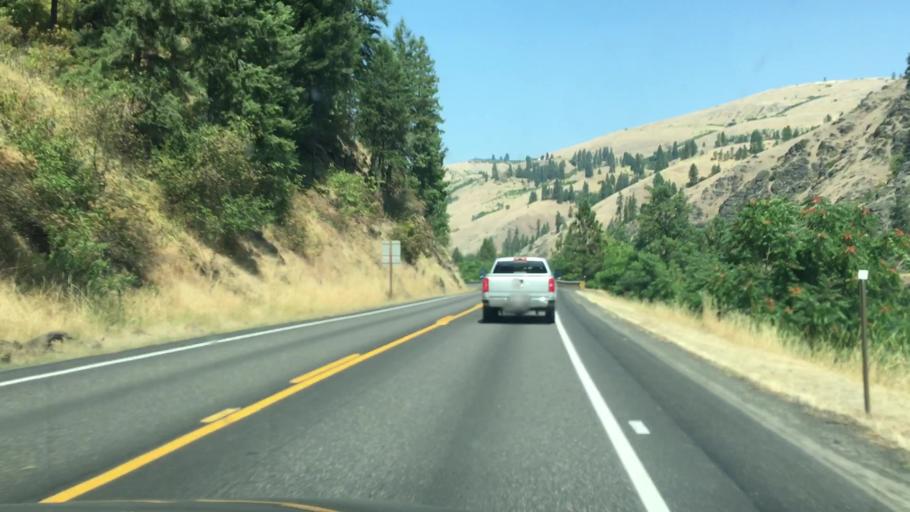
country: US
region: Idaho
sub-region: Clearwater County
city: Orofino
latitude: 46.4926
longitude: -116.4597
